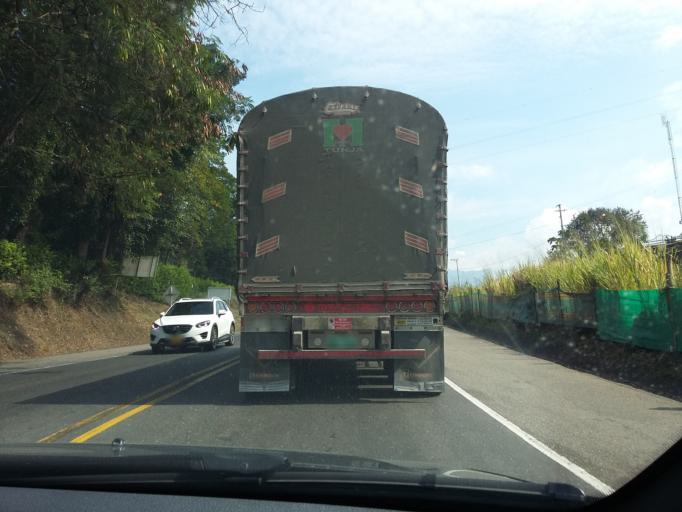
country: CO
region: Tolima
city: Ibague
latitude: 4.4063
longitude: -75.1837
